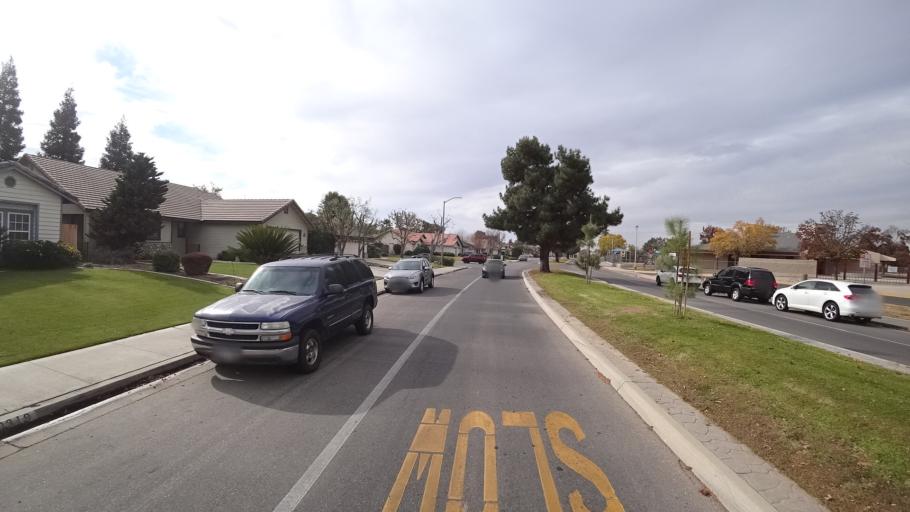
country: US
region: California
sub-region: Kern County
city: Greenacres
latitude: 35.3907
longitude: -119.1061
